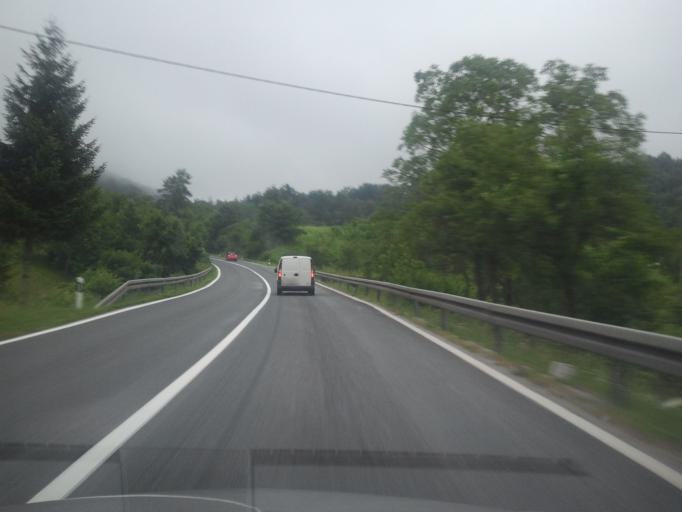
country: HR
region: Karlovacka
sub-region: Grad Karlovac
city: Slunj
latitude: 45.1886
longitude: 15.5597
